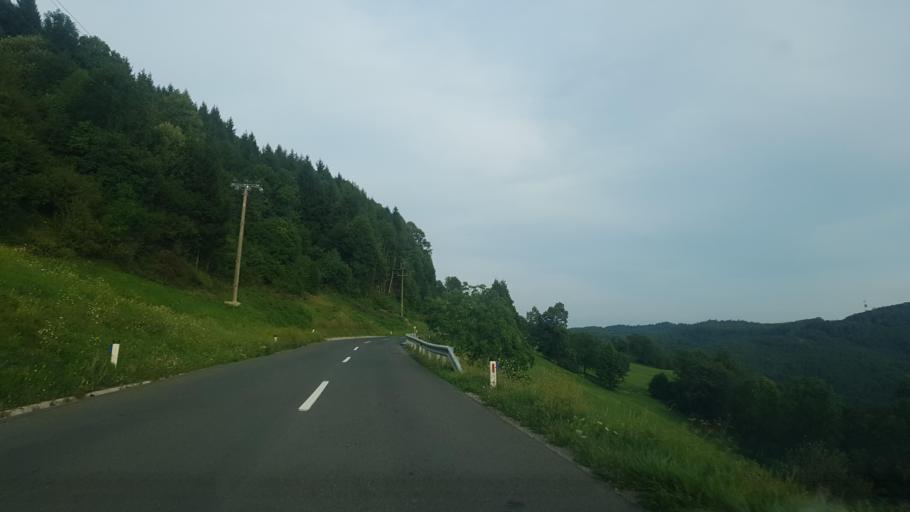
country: SI
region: Vipava
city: Vipava
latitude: 45.8705
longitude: 14.0388
